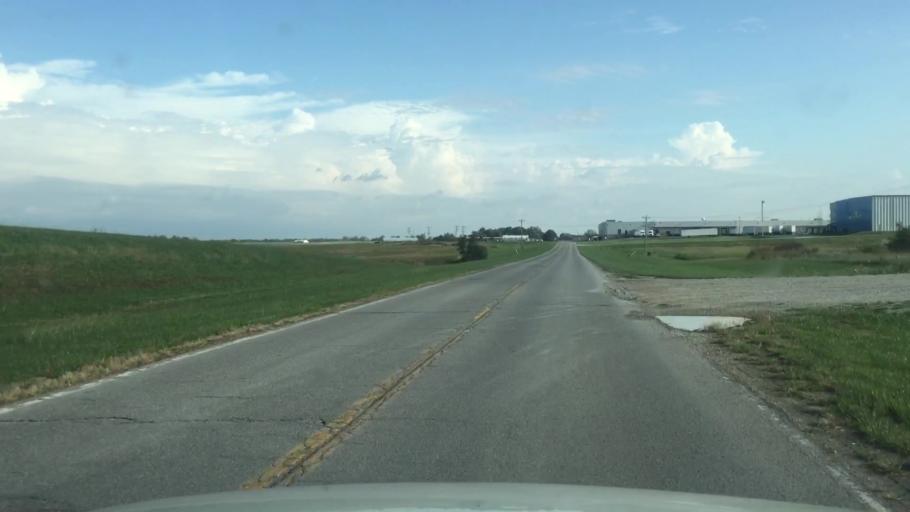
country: US
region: Missouri
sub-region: Boone County
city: Ashland
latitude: 38.8109
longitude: -92.2265
